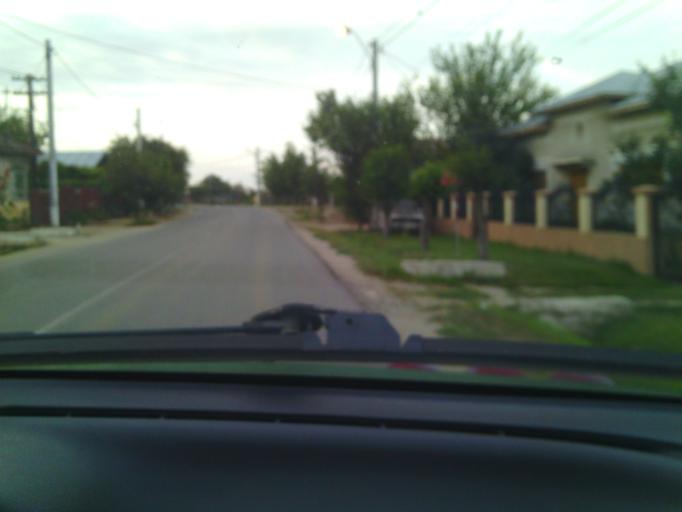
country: RO
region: Giurgiu
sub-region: Comuna Varasti
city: Varasti
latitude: 44.2184
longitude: 26.2578
